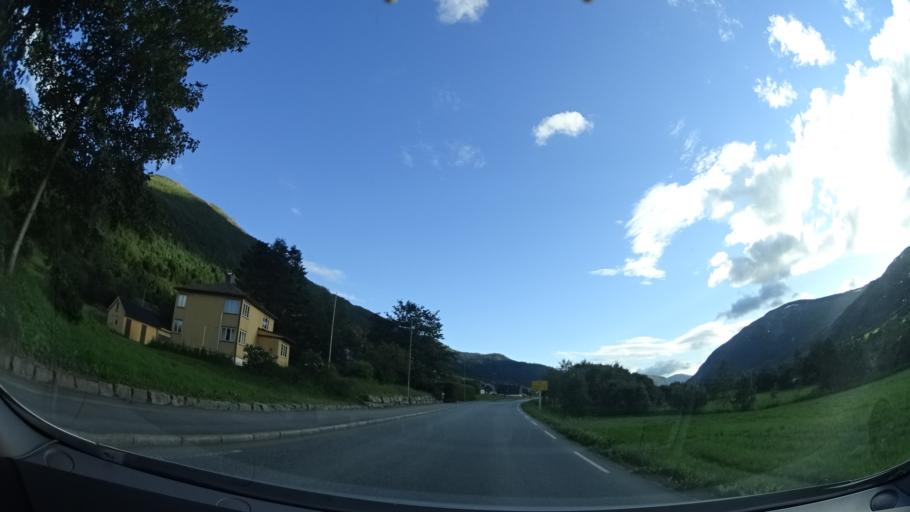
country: NO
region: More og Romsdal
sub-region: Gjemnes
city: Batnfjordsora
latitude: 62.8906
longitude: 7.6784
